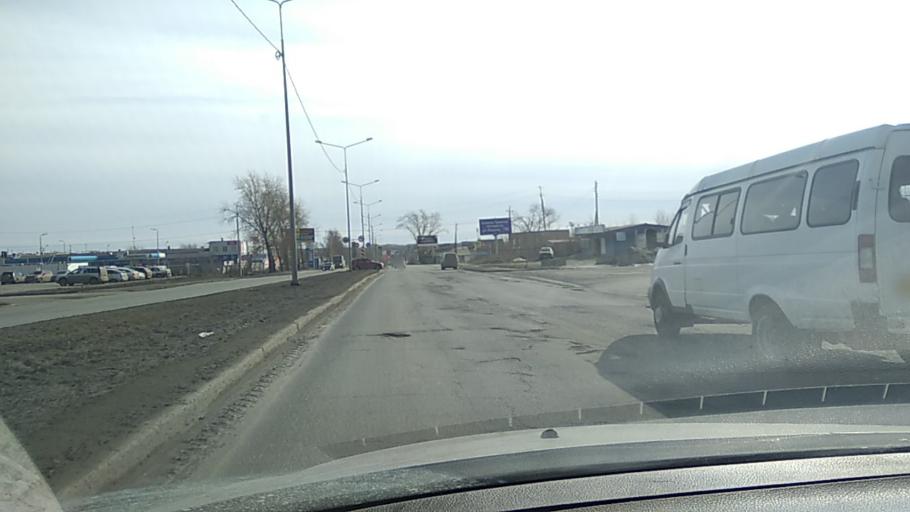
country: RU
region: Sverdlovsk
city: Nizhniy Tagil
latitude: 57.9068
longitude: 60.0091
